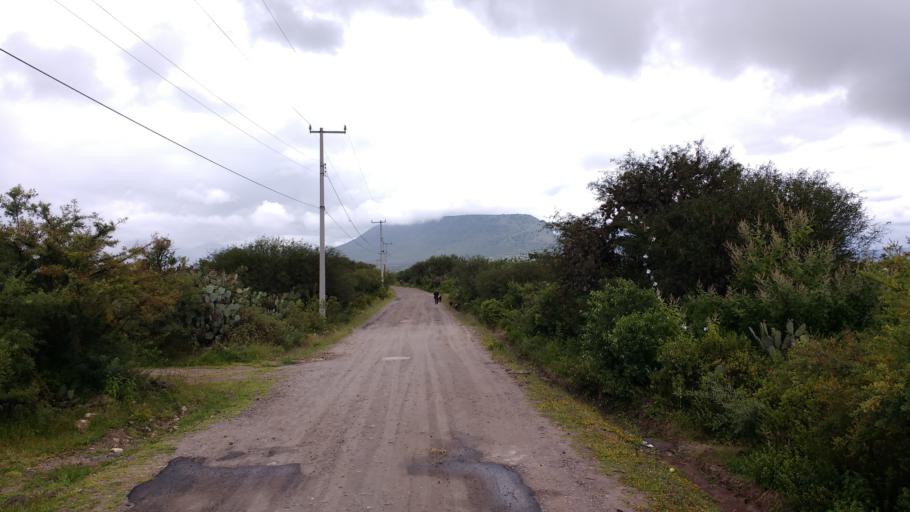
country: MX
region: Hidalgo
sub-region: Tezontepec de Aldama
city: Tenango
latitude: 20.2760
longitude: -99.2838
